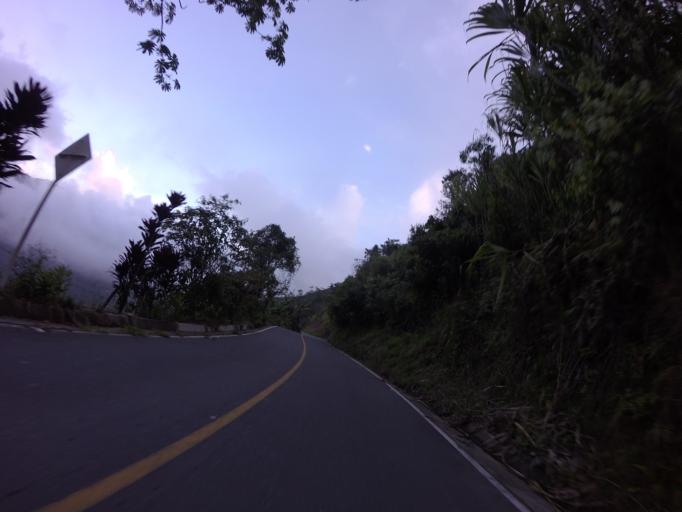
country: CO
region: Caldas
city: Manzanares
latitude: 5.3472
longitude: -75.1166
